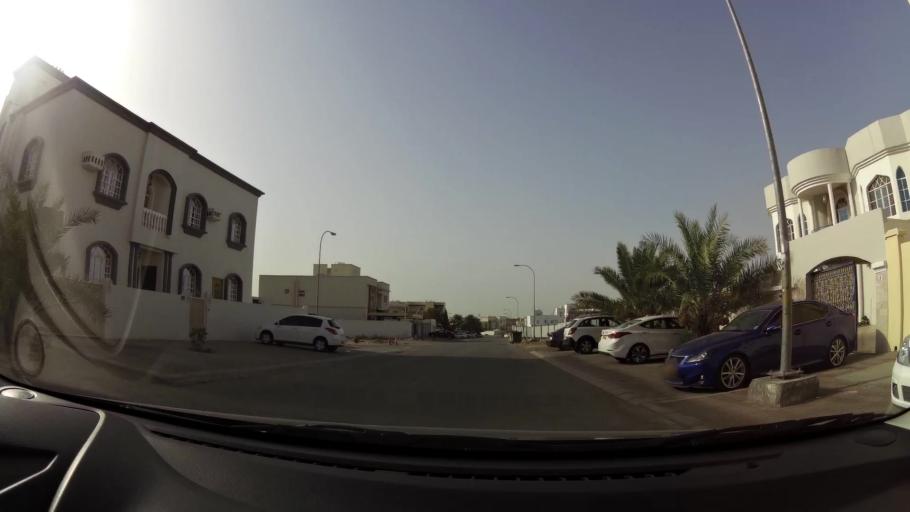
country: OM
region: Muhafazat Masqat
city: Bawshar
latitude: 23.5408
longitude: 58.3602
